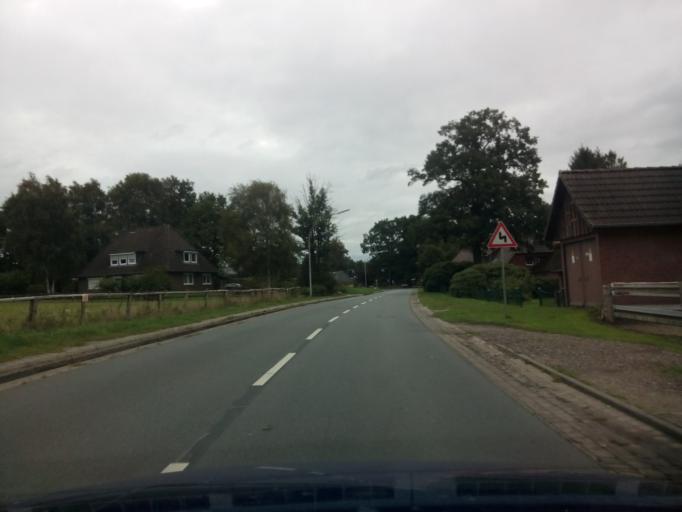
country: DE
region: Lower Saxony
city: Osterholz-Scharmbeck
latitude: 53.2446
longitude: 8.8111
